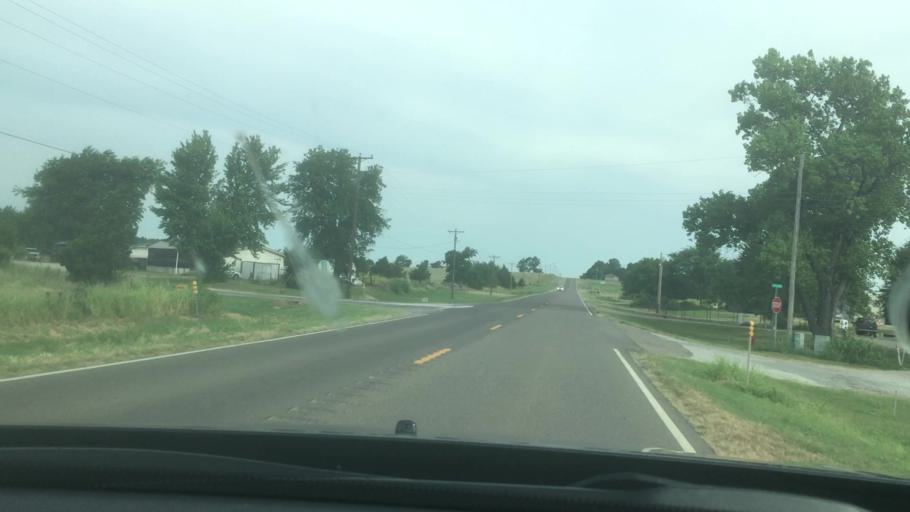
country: US
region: Oklahoma
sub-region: Garvin County
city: Pauls Valley
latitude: 34.7533
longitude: -97.2899
